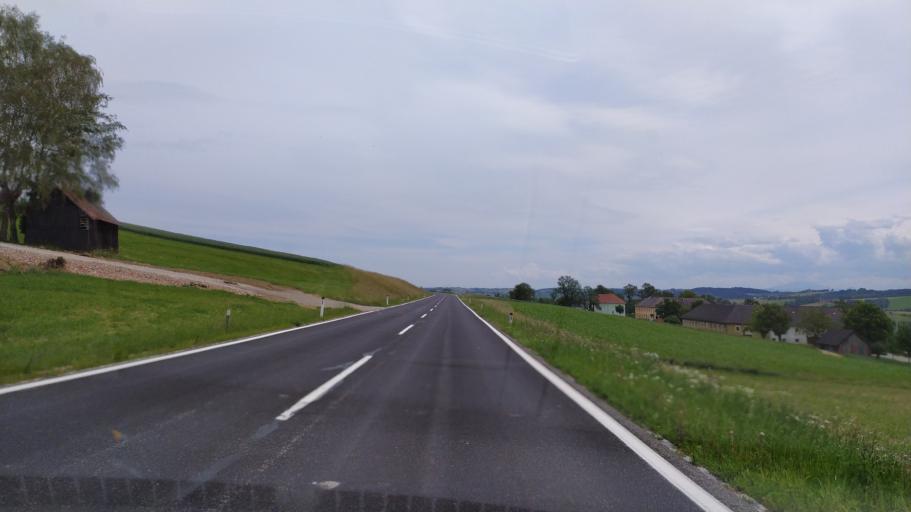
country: AT
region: Lower Austria
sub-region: Politischer Bezirk Amstetten
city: Strengberg
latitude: 48.1388
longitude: 14.6172
